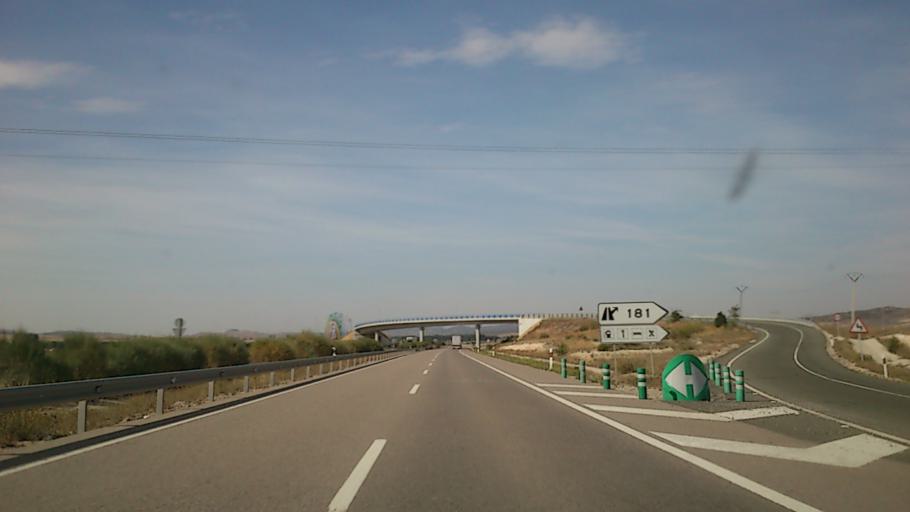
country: ES
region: Aragon
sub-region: Provincia de Teruel
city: Fuentes Claras
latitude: 40.8846
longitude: -1.3059
